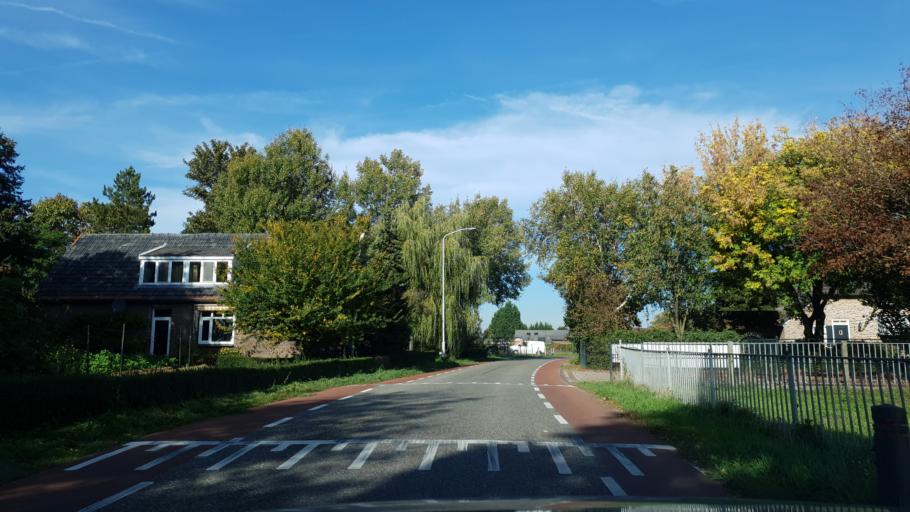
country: NL
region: Gelderland
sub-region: Gemeente Wijchen
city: Bergharen
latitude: 51.8615
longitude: 5.6532
